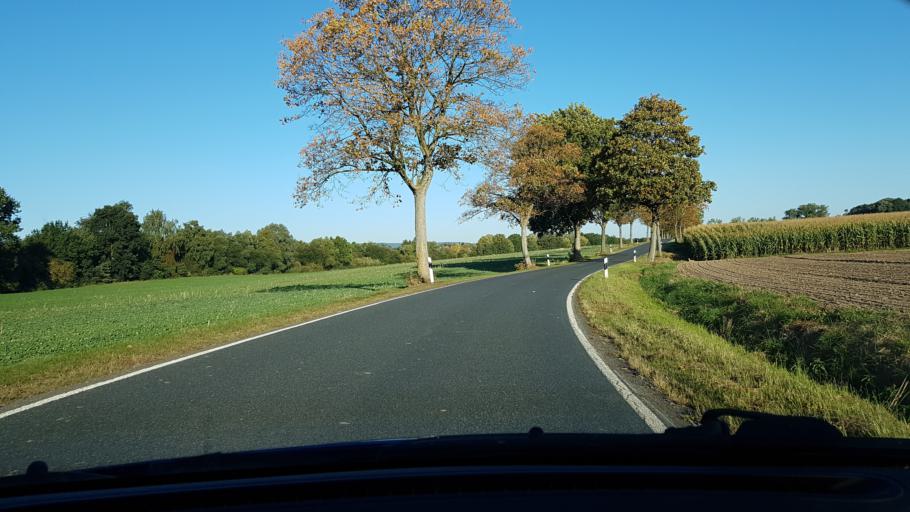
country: DE
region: Lower Saxony
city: Bad Munder am Deister
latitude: 52.2116
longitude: 9.4126
